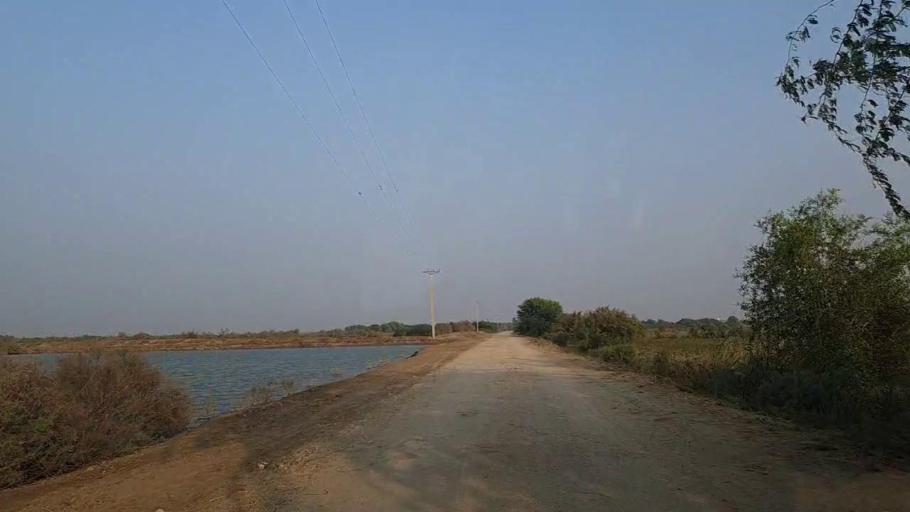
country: PK
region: Sindh
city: Thatta
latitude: 24.6921
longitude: 67.8034
